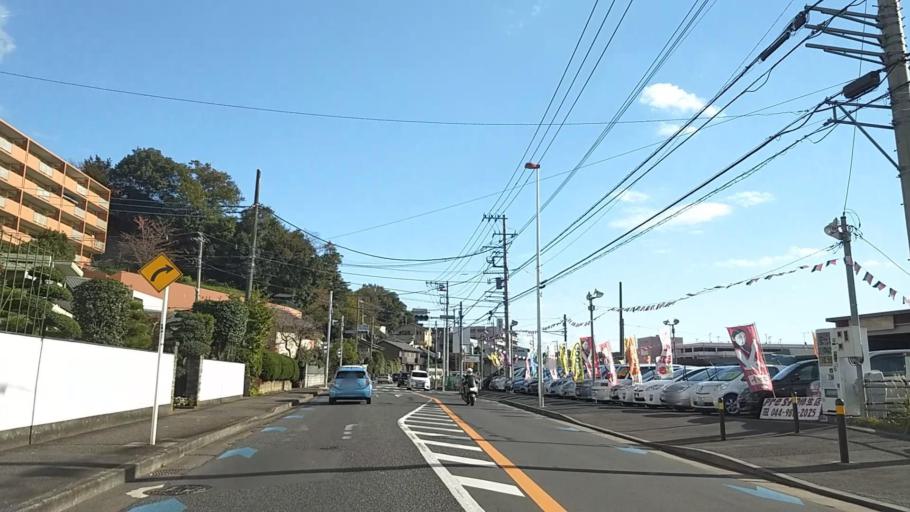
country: JP
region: Tokyo
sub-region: Machida-shi
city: Machida
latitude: 35.5817
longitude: 139.4990
